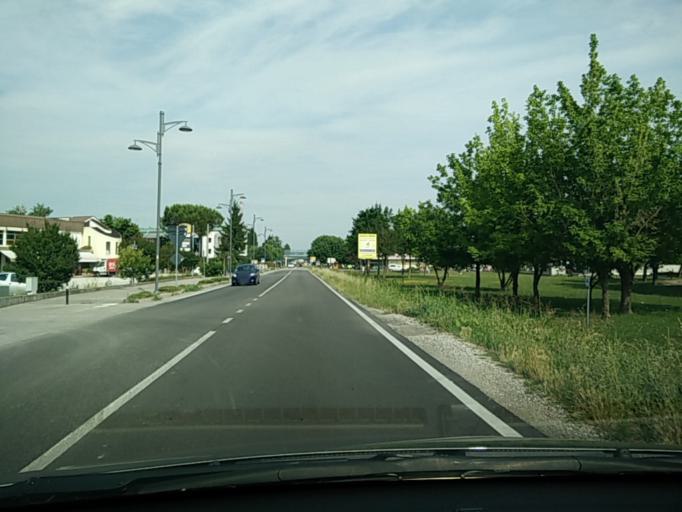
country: IT
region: Veneto
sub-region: Provincia di Treviso
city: Musestre
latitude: 45.5837
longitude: 12.3547
